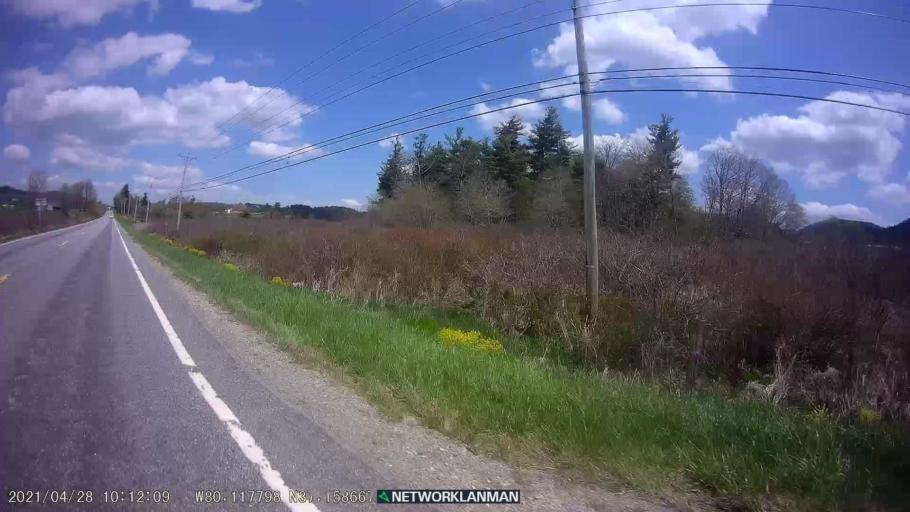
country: US
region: Virginia
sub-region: Roanoke County
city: Cave Spring
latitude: 37.1592
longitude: -80.1177
